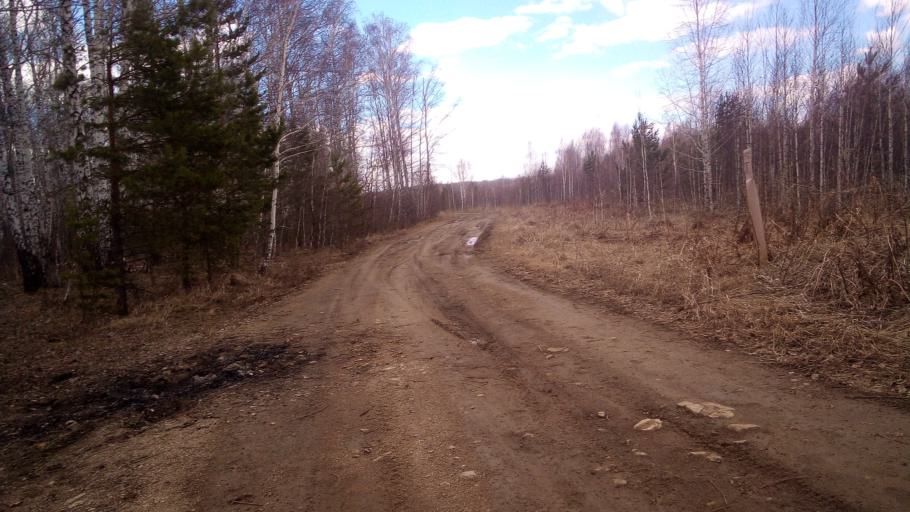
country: RU
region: Chelyabinsk
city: Sargazy
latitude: 55.1229
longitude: 61.2512
